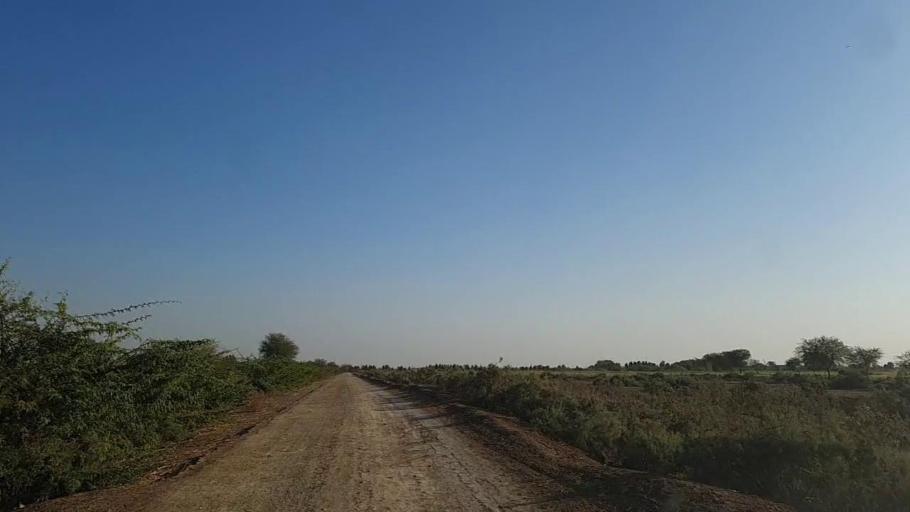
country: PK
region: Sindh
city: Samaro
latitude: 25.3351
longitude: 69.4114
